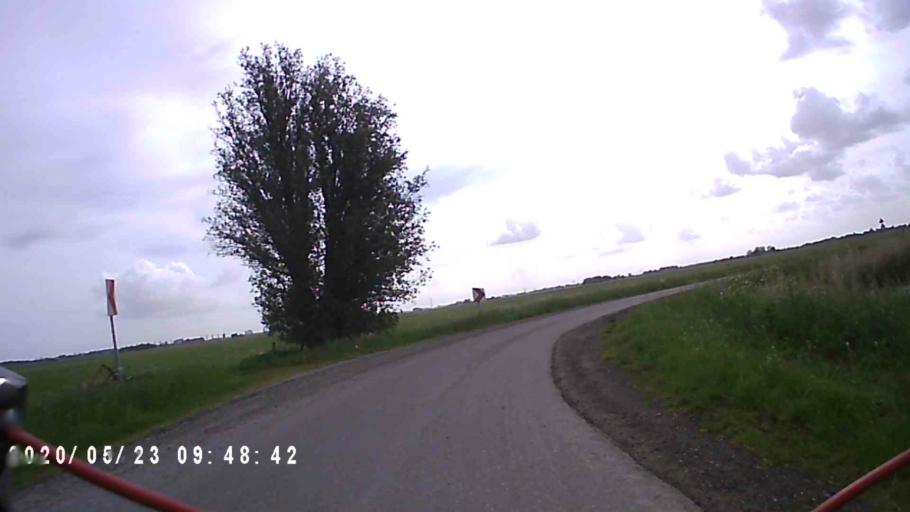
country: NL
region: Groningen
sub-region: Gemeente Slochteren
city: Slochteren
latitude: 53.2928
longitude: 6.7619
